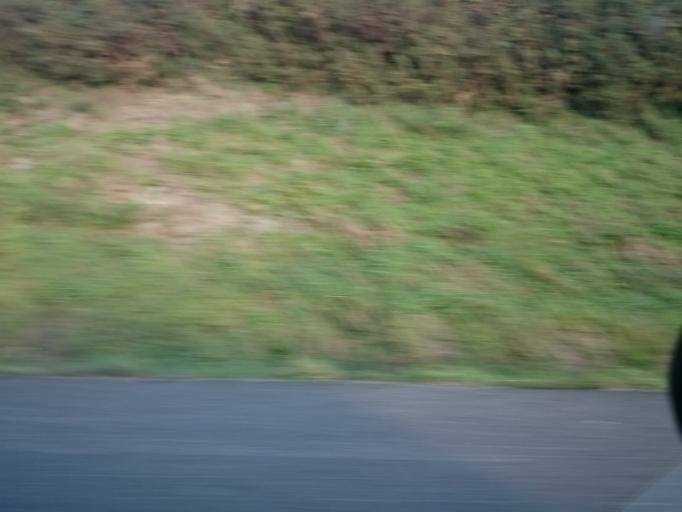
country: FR
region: Brittany
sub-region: Departement d'Ille-et-Vilaine
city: Pance
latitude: 47.8874
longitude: -1.6903
